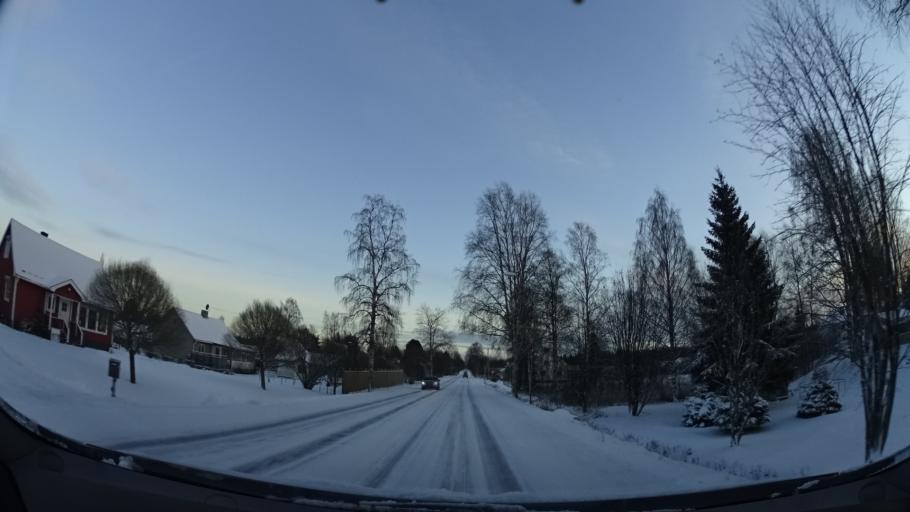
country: SE
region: Vaesterbotten
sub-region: Skelleftea Kommun
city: Kage
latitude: 64.8319
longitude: 20.9933
